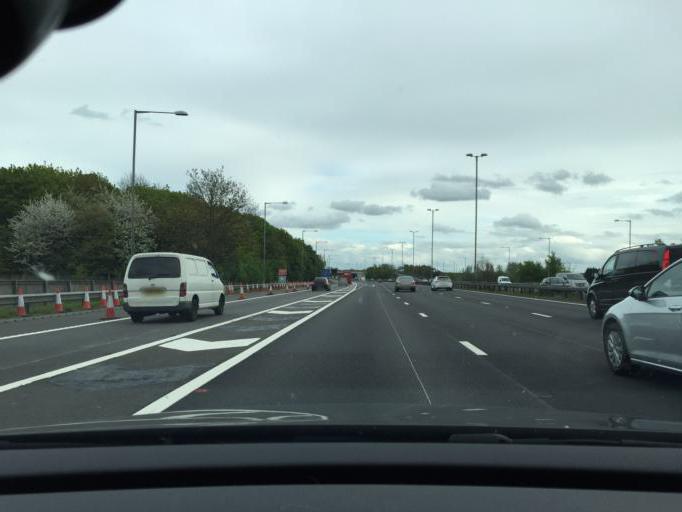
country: GB
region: England
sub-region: Wokingham
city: Shinfield
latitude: 51.4154
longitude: -0.9806
